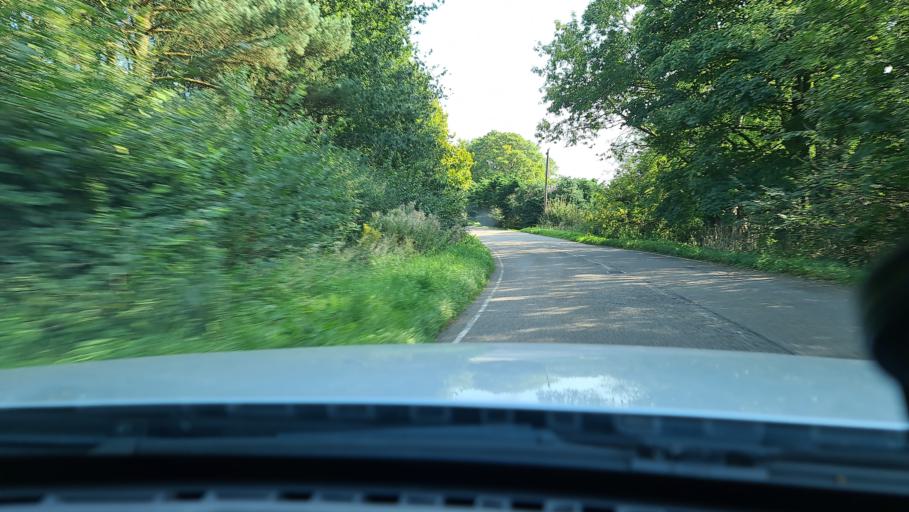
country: GB
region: England
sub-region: Northamptonshire
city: Daventry
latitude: 52.1531
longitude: -1.1453
